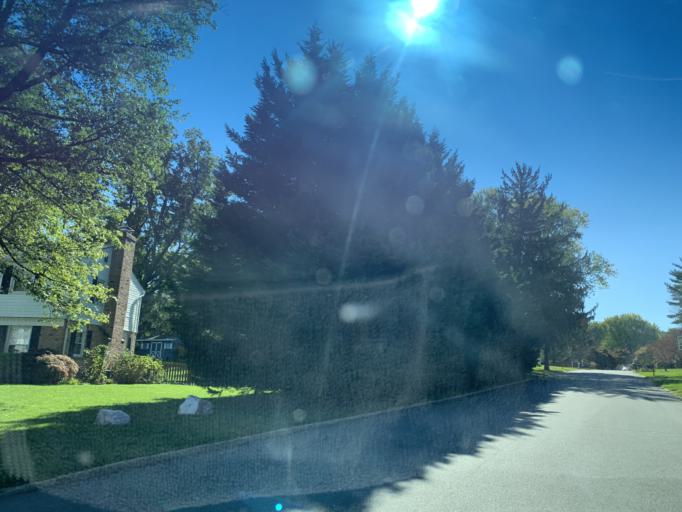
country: US
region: Maryland
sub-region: Harford County
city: South Bel Air
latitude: 39.5199
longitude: -76.3276
